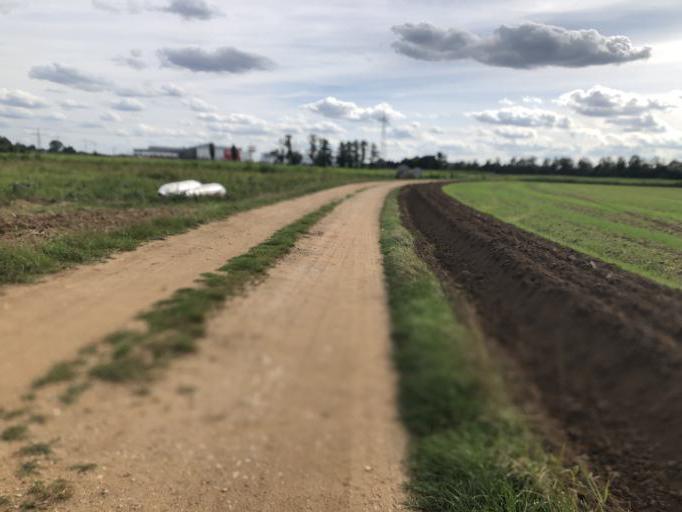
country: DE
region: Bavaria
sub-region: Regierungsbezirk Mittelfranken
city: Furth
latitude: 49.5272
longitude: 10.9968
